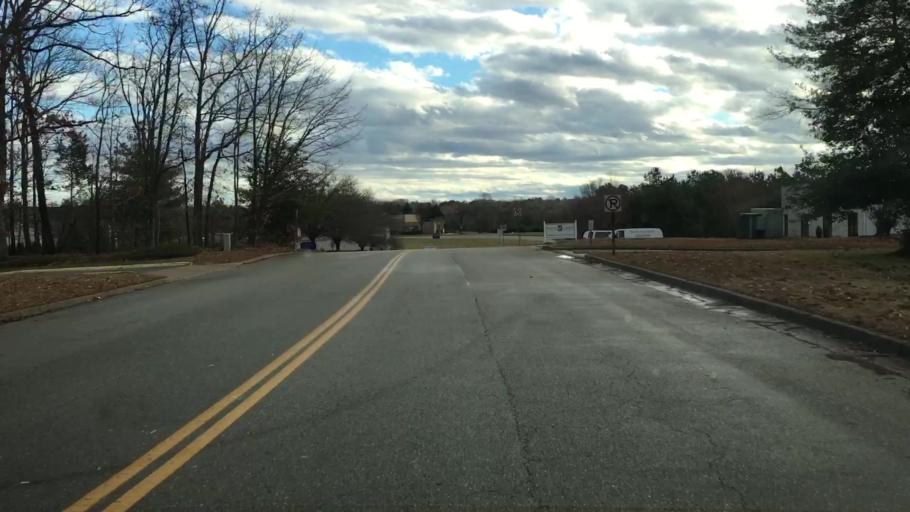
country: US
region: Virginia
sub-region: Chesterfield County
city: Bon Air
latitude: 37.5000
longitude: -77.5941
